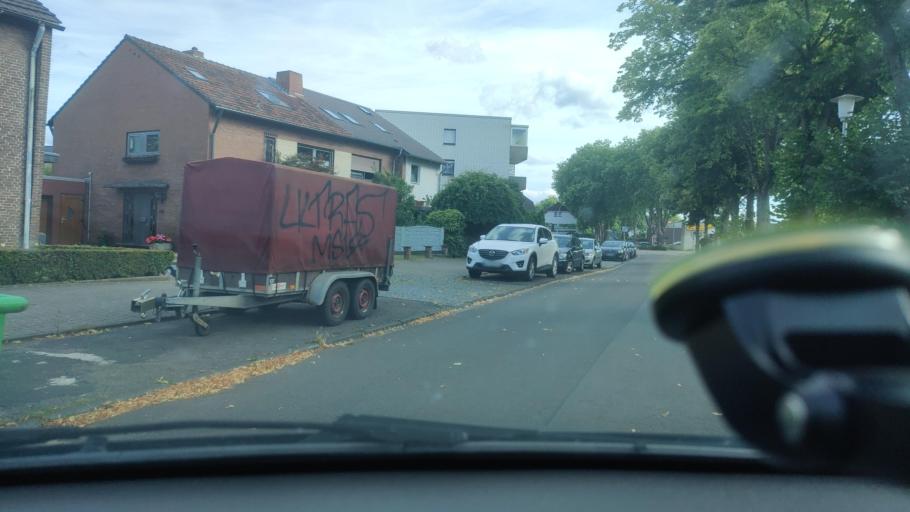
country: DE
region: North Rhine-Westphalia
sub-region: Regierungsbezirk Dusseldorf
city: Kamp-Lintfort
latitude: 51.5010
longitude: 6.5611
